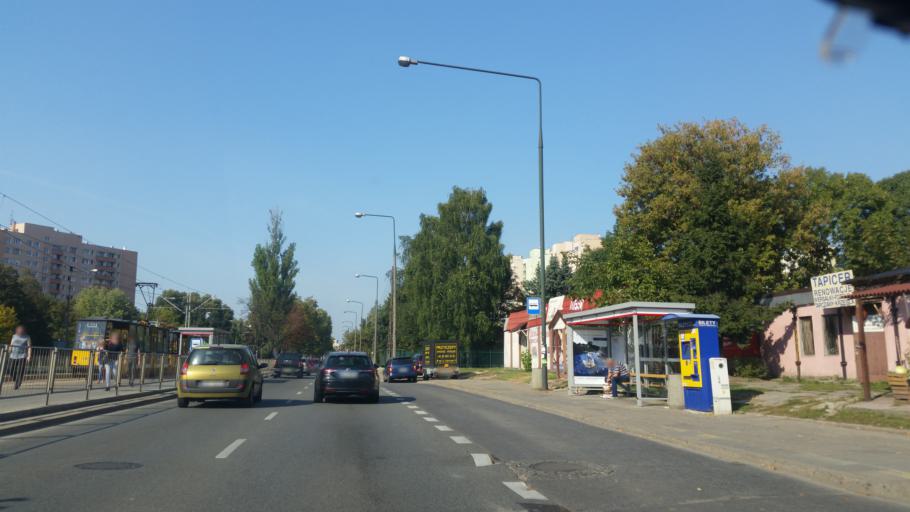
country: PL
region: Masovian Voivodeship
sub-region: Warszawa
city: Bemowo
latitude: 52.2254
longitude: 20.9166
